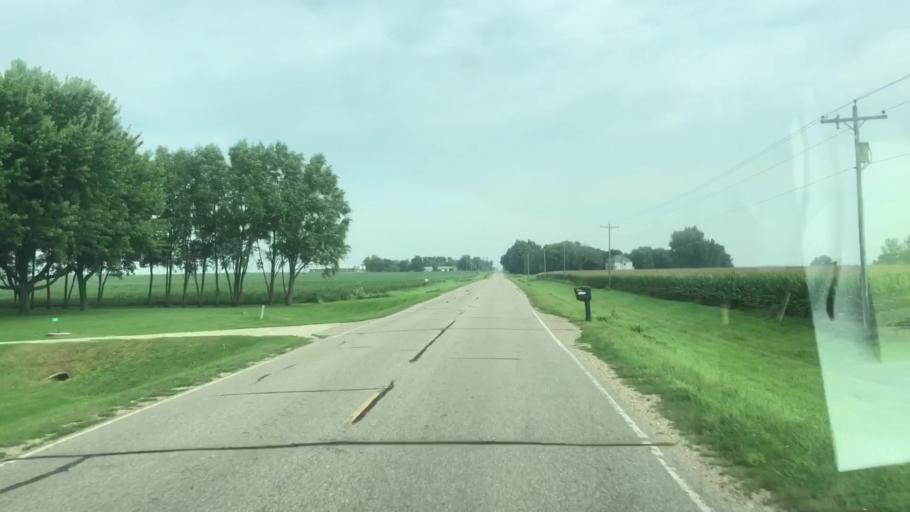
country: US
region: Iowa
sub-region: O'Brien County
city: Sheldon
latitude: 43.1971
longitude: -95.8622
